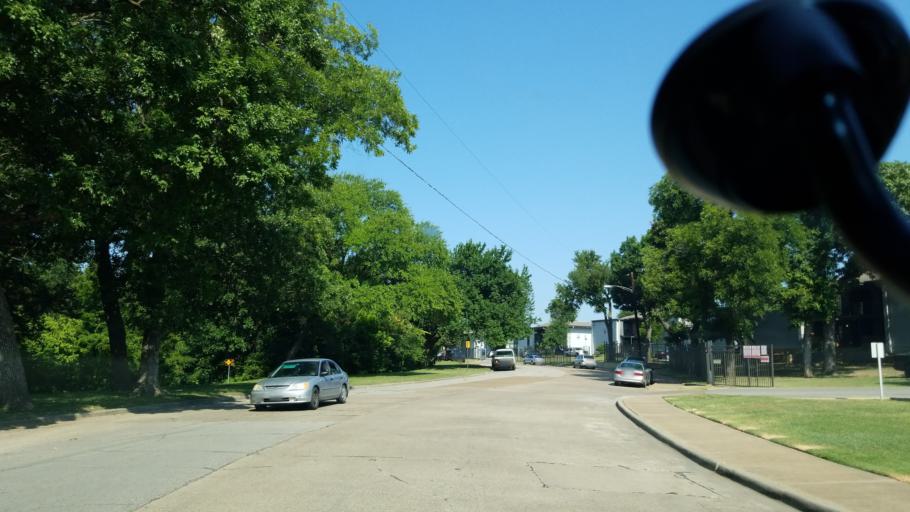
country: US
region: Texas
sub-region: Dallas County
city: Cockrell Hill
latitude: 32.7061
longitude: -96.8716
